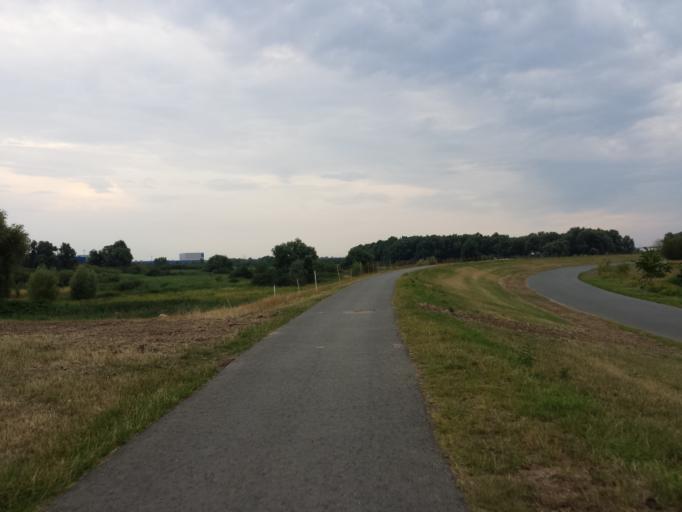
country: DE
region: Lower Saxony
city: Ritterhude
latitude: 53.1103
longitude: 8.7275
